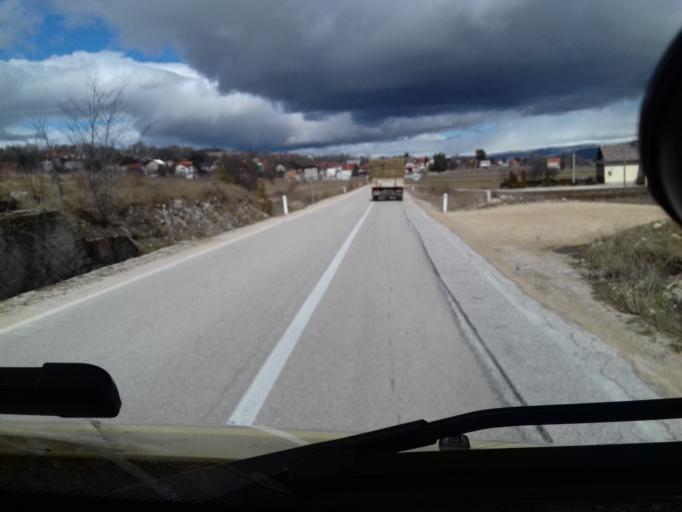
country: BA
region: Federation of Bosnia and Herzegovina
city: Dreznica
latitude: 43.5914
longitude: 17.2737
